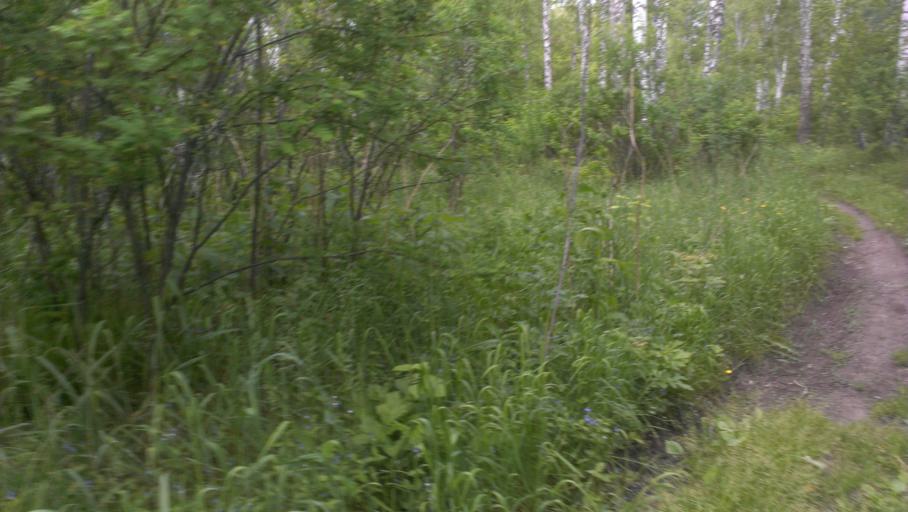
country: RU
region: Altai Krai
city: Sannikovo
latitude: 53.3429
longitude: 84.0600
